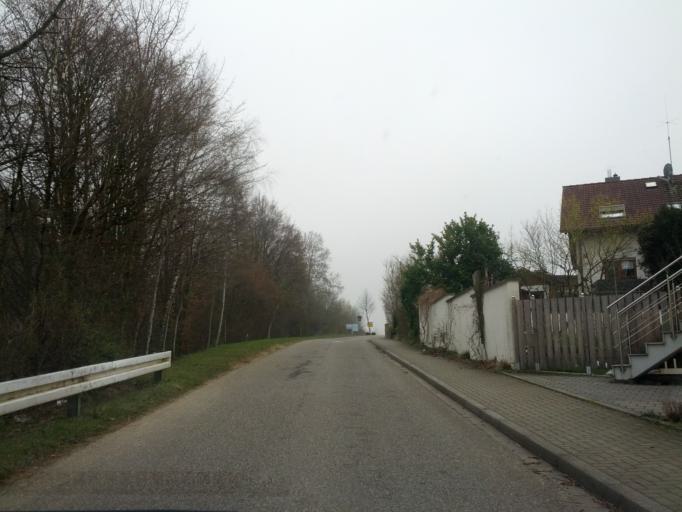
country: DE
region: Baden-Wuerttemberg
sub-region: Freiburg Region
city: Solden
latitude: 47.9413
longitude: 7.8169
